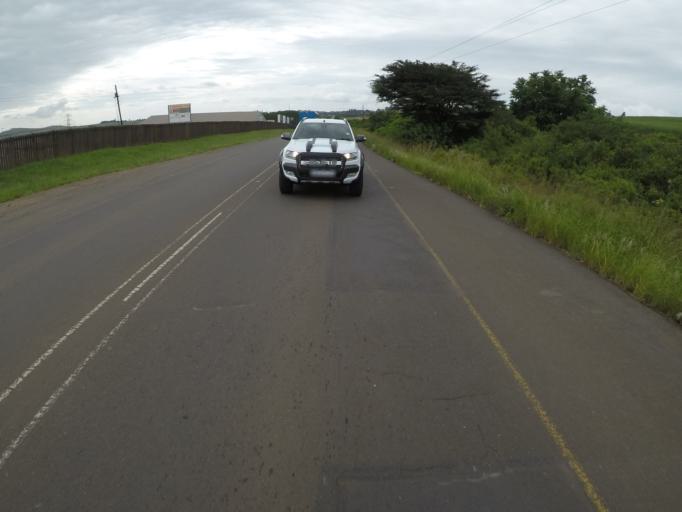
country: ZA
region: KwaZulu-Natal
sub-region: uThungulu District Municipality
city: Empangeni
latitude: -28.7263
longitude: 31.8677
